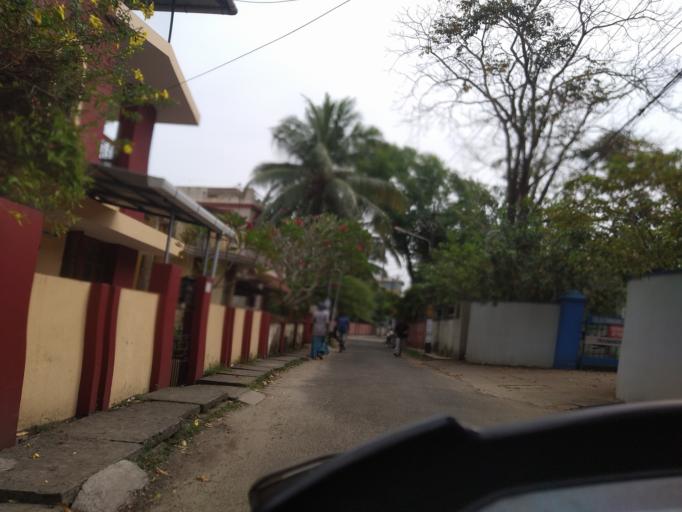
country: IN
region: Kerala
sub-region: Ernakulam
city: Cochin
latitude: 9.9499
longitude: 76.2943
